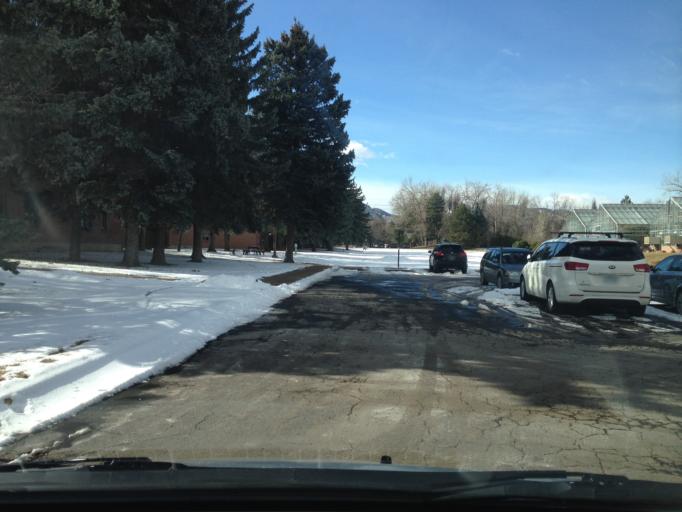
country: US
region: Colorado
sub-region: Boulder County
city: Boulder
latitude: 40.0103
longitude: -105.2515
